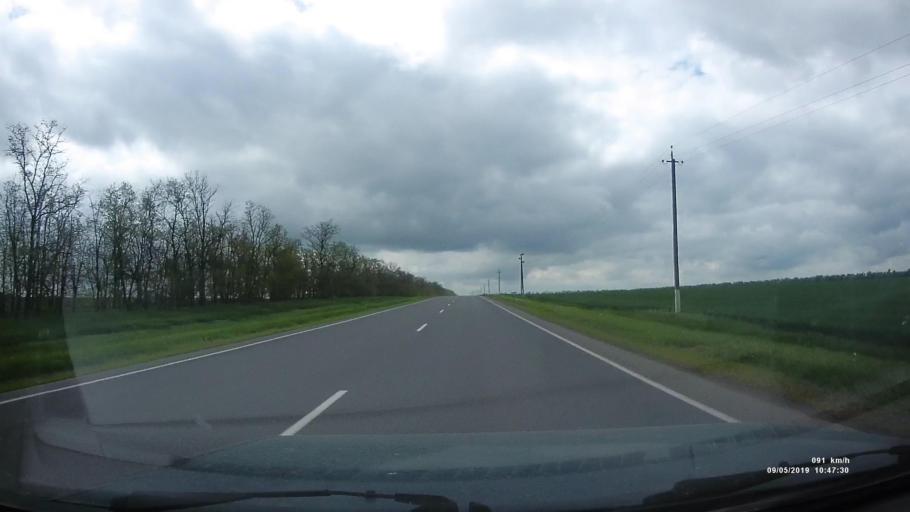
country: RU
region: Rostov
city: Peshkovo
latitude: 46.9698
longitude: 39.3556
